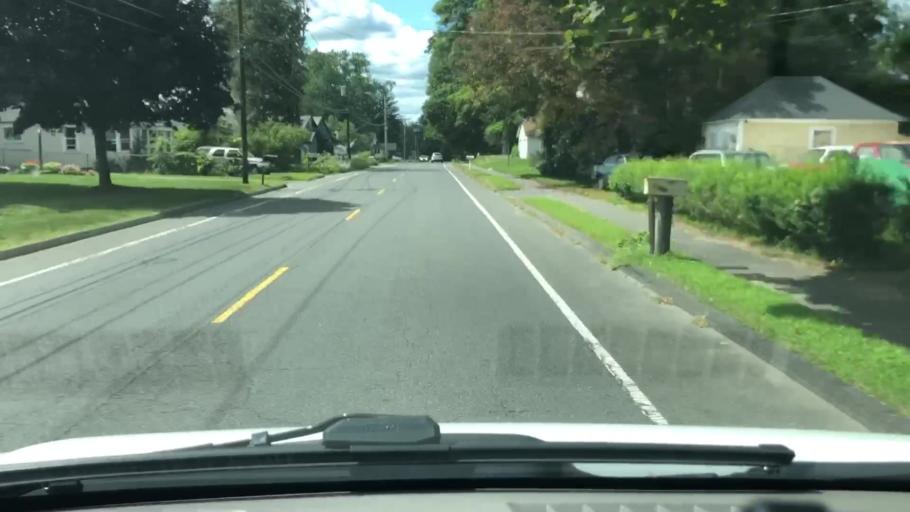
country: US
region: Massachusetts
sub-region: Hampshire County
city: Hatfield
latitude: 42.3603
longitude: -72.6244
